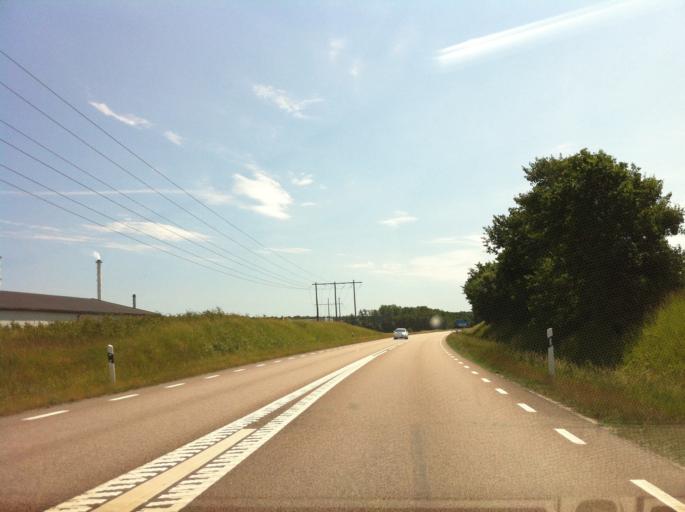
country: SE
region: Skane
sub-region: Bjuvs Kommun
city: Bjuv
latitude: 56.0656
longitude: 12.9451
